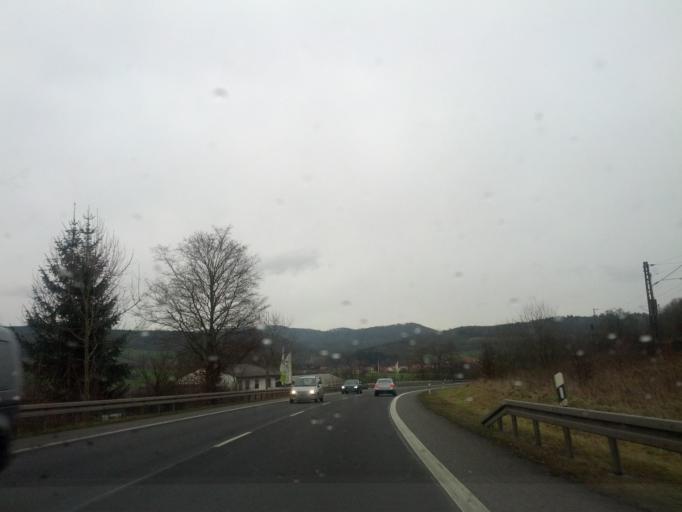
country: DE
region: Thuringia
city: Wahlhausen
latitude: 51.2990
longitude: 9.9626
